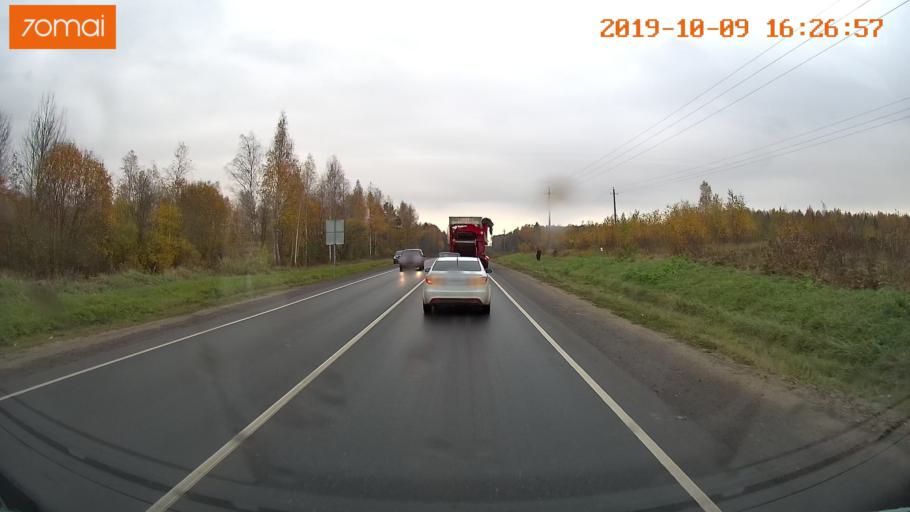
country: RU
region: Kostroma
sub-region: Kostromskoy Rayon
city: Kostroma
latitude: 57.6353
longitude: 40.9262
